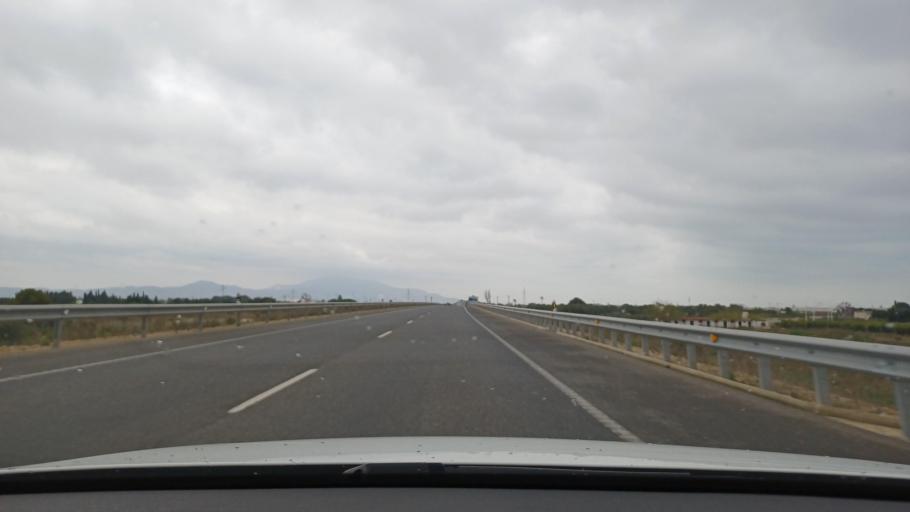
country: ES
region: Valencia
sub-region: Provincia de Castello
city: Vinaros
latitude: 40.4857
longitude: 0.4529
